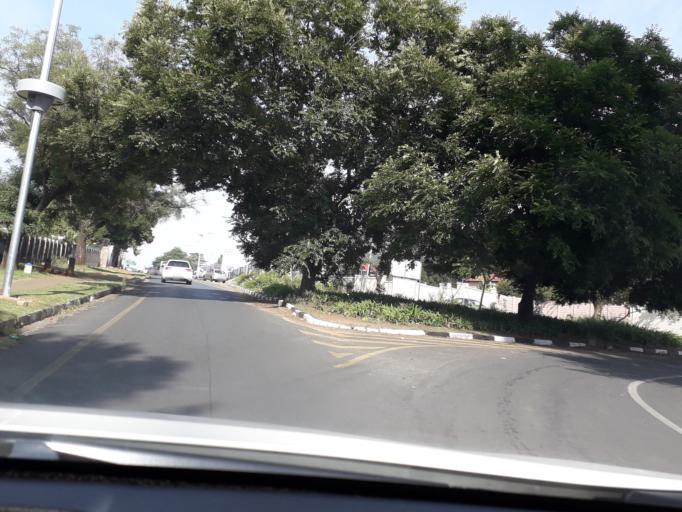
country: ZA
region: Gauteng
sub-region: City of Johannesburg Metropolitan Municipality
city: Modderfontein
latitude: -26.1254
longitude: 28.0875
